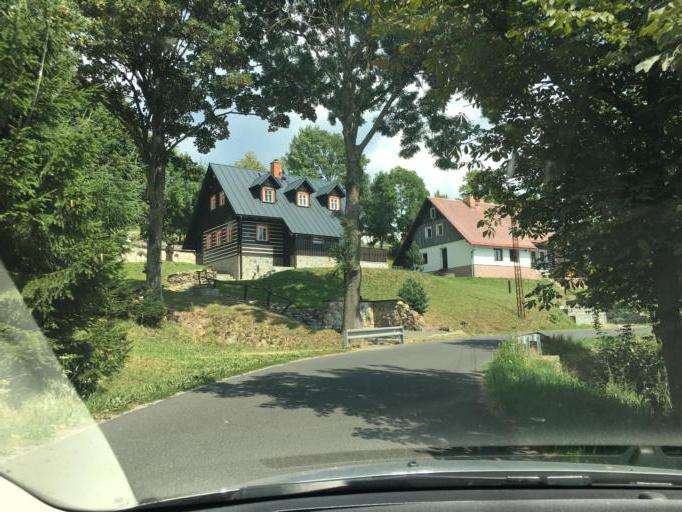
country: CZ
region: Liberecky
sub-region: Okres Semily
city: Ponikla
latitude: 50.6829
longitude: 15.4978
